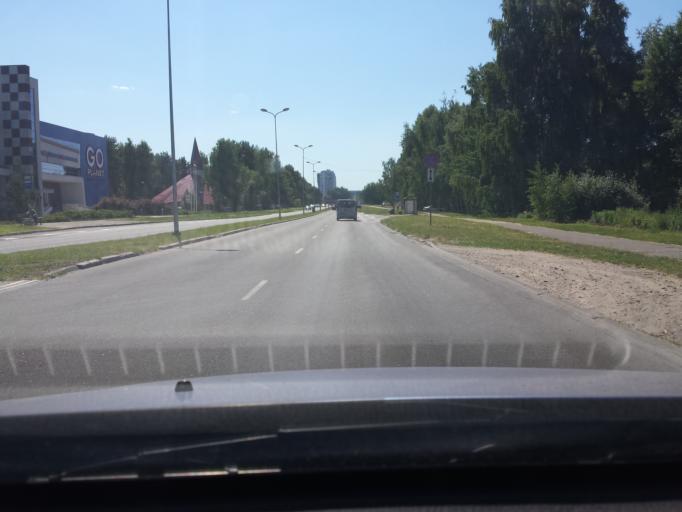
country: LV
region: Riga
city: Jaunciems
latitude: 56.9619
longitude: 24.1987
